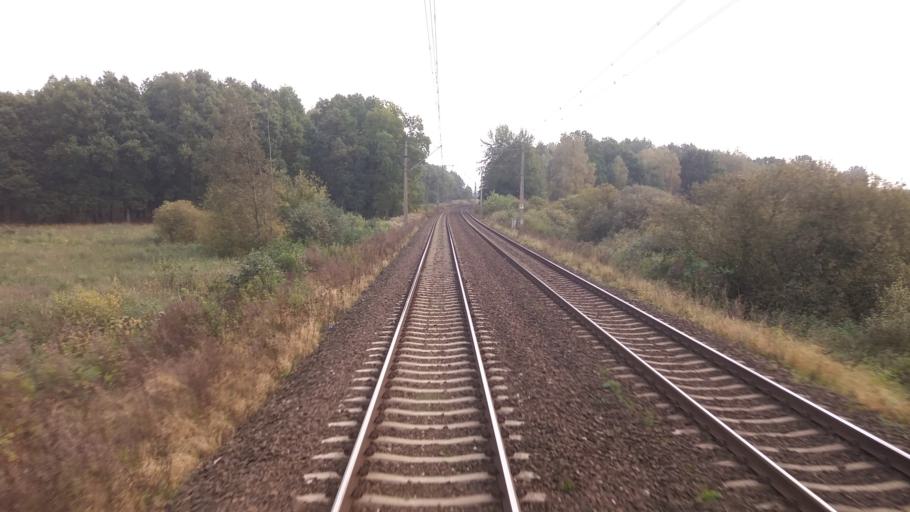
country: PL
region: West Pomeranian Voivodeship
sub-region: Powiat stargardzki
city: Dolice
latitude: 53.2067
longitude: 15.1796
